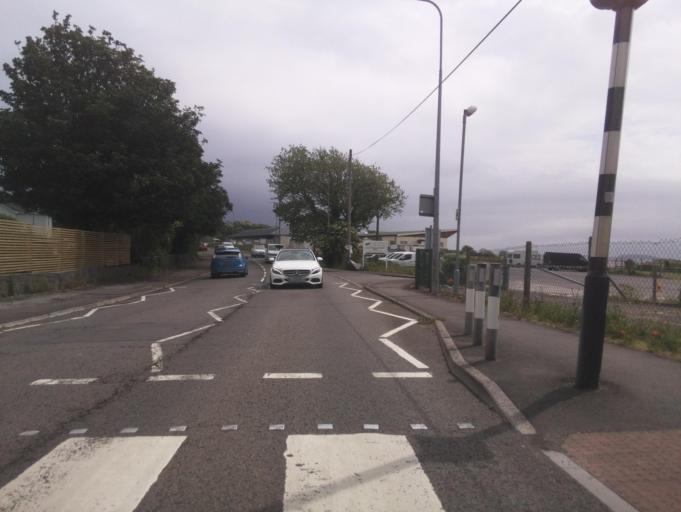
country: GB
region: Wales
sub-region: Vale of Glamorgan
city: Dinas Powys
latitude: 51.4040
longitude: -3.2077
